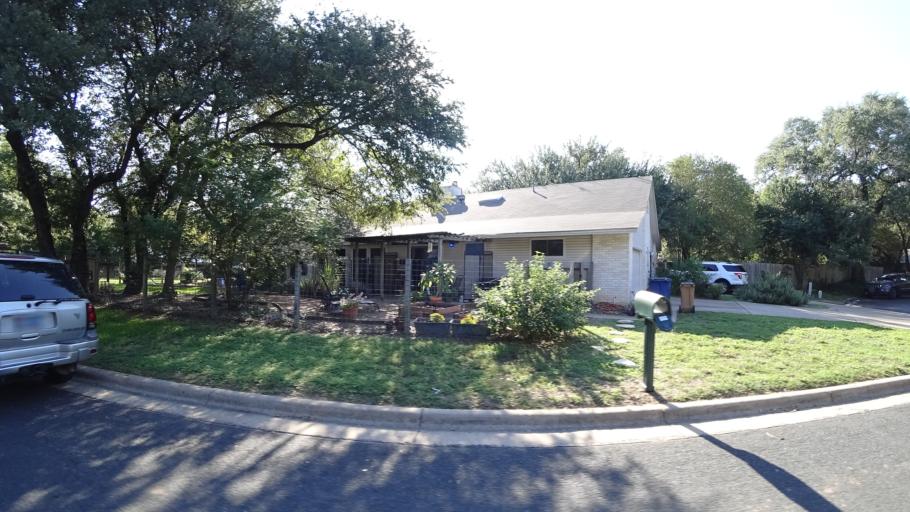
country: US
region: Texas
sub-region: Travis County
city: Rollingwood
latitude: 30.2679
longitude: -97.8046
